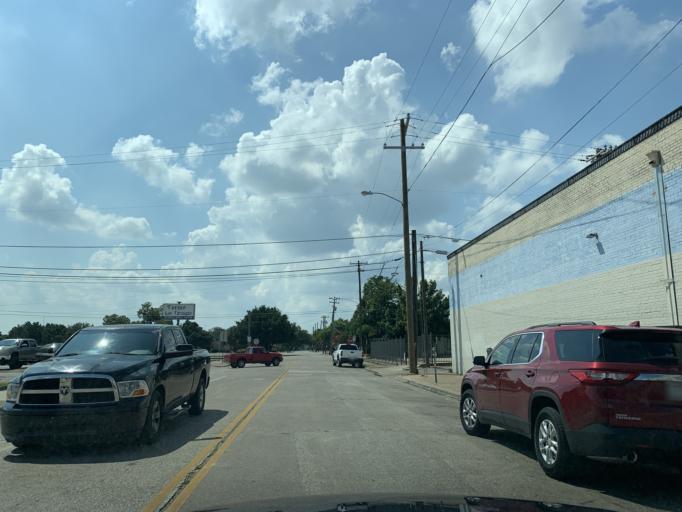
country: US
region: Texas
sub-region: Dallas County
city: Dallas
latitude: 32.7429
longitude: -96.8265
